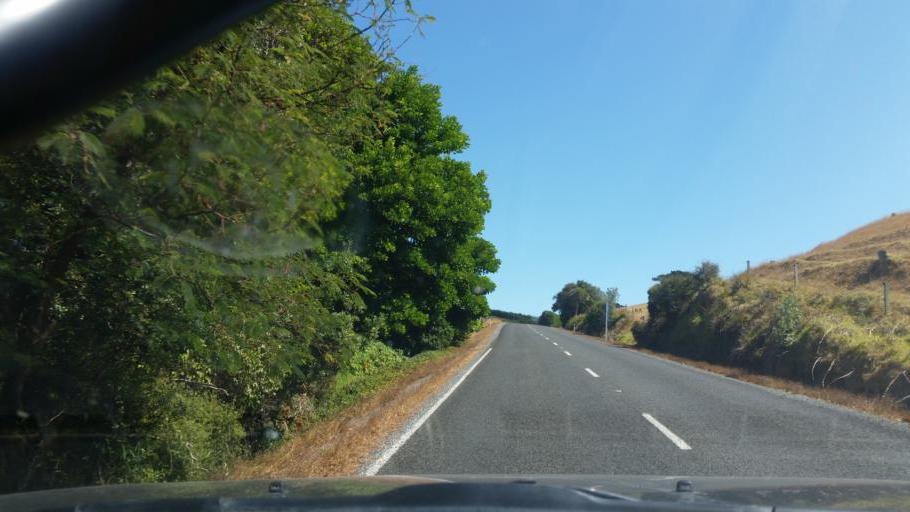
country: NZ
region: Northland
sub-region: Kaipara District
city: Dargaville
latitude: -35.9449
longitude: 173.7731
